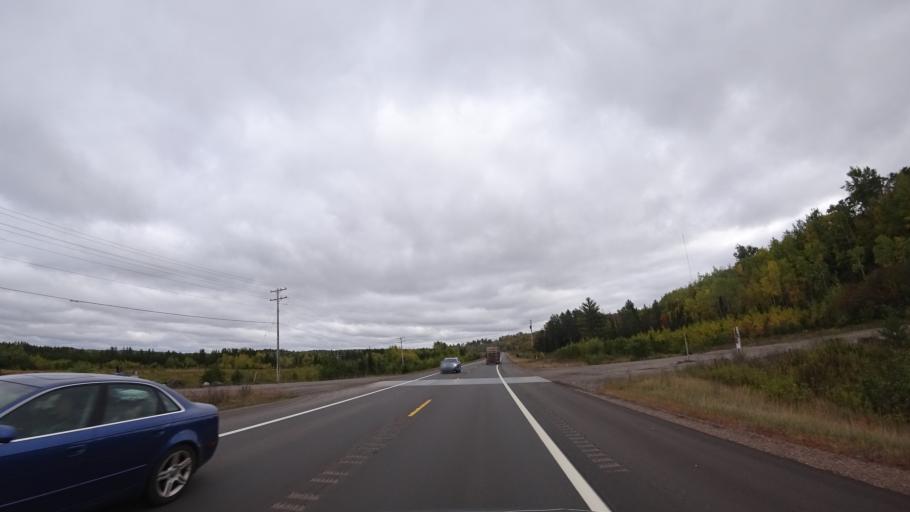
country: US
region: Michigan
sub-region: Marquette County
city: West Ishpeming
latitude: 46.4976
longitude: -87.9022
